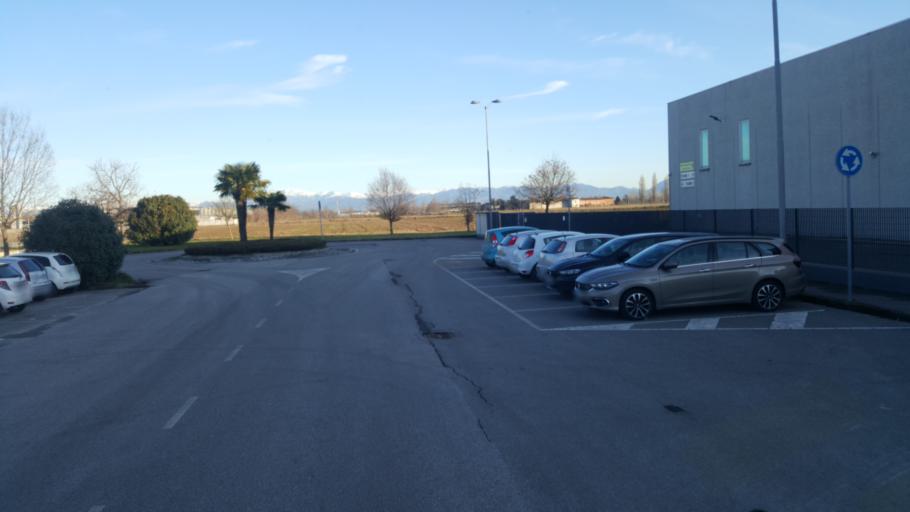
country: IT
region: Lombardy
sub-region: Provincia di Brescia
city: Barbariga
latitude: 45.3945
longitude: 10.0711
